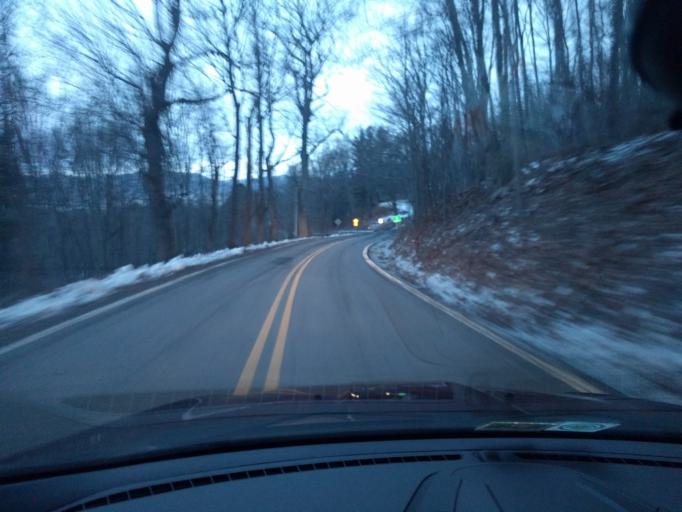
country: US
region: Virginia
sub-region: Alleghany County
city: Clifton Forge
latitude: 37.8925
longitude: -79.8871
